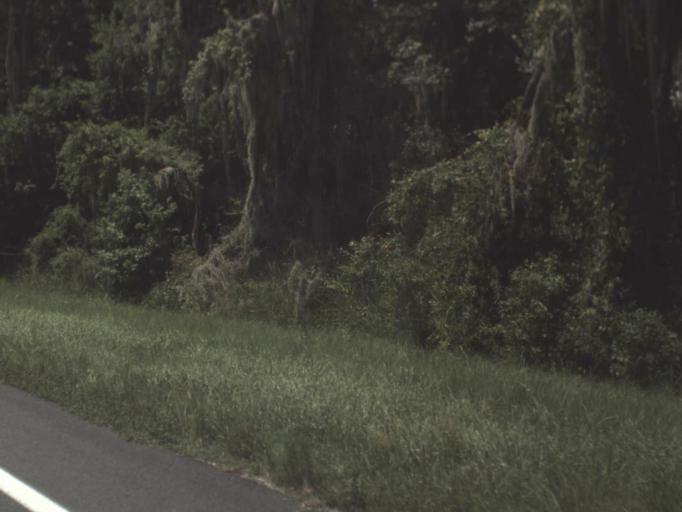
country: US
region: Florida
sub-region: Hamilton County
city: Jasper
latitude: 30.4163
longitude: -82.8516
